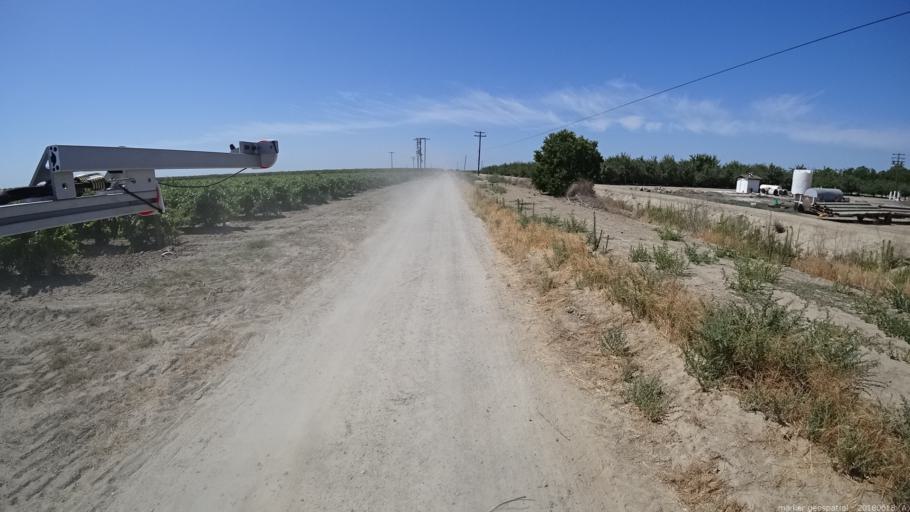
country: US
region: California
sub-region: Madera County
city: Parkwood
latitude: 36.8536
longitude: -120.2010
